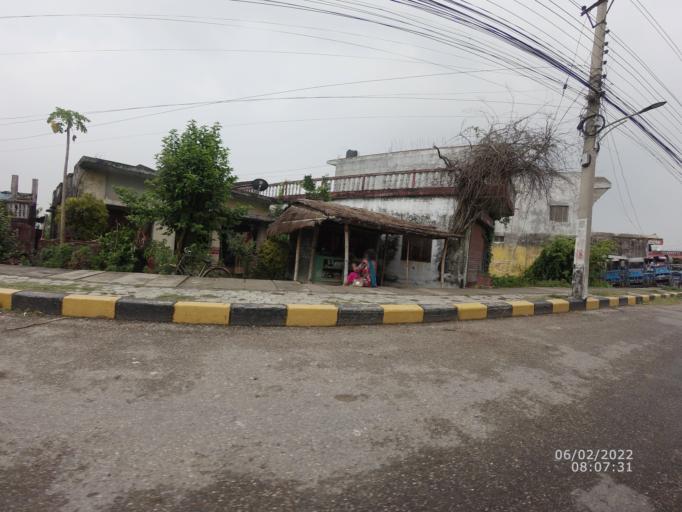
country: NP
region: Western Region
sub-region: Lumbini Zone
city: Bhairahawa
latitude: 27.4833
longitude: 83.4623
